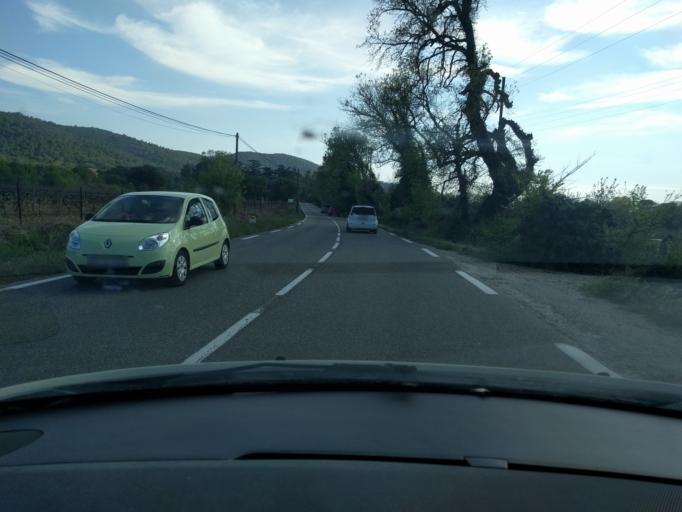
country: FR
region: Provence-Alpes-Cote d'Azur
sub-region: Departement du Var
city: Pierrefeu-du-Var
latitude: 43.2013
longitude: 6.1346
